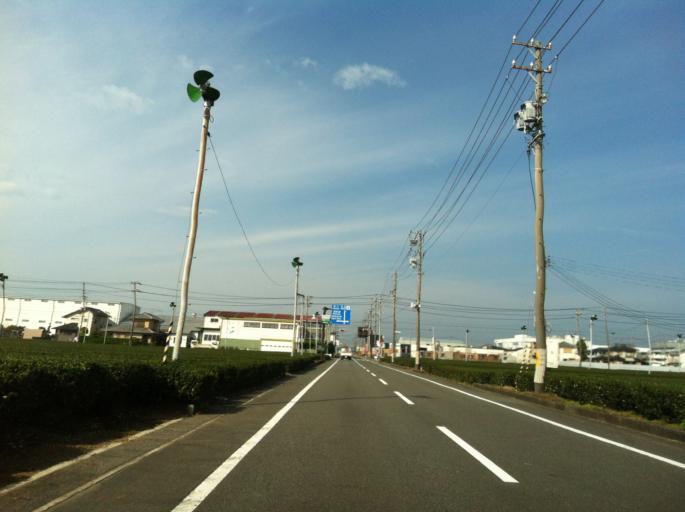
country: JP
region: Shizuoka
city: Kanaya
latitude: 34.7734
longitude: 138.1486
